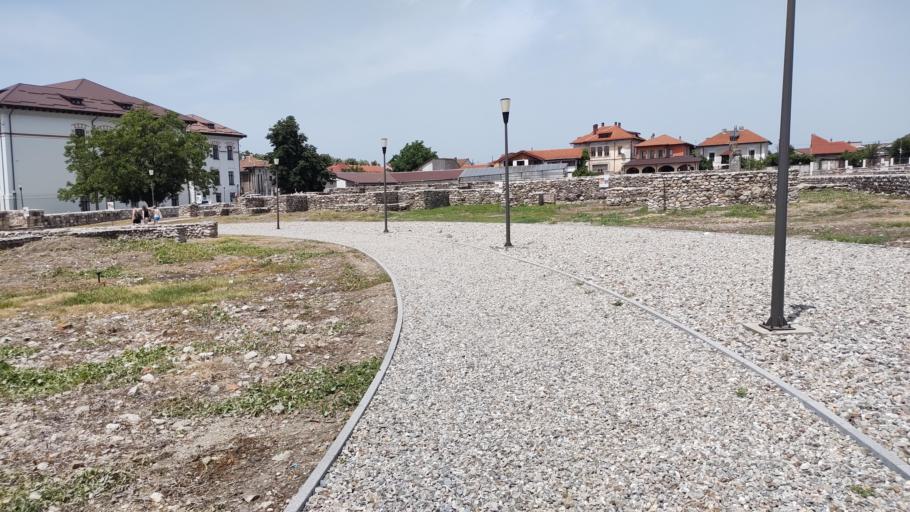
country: RO
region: Mehedinti
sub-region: Municipiul Drobeta-Turnu Severin
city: Drobeta-Turnu Severin
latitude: 44.6244
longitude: 22.6680
